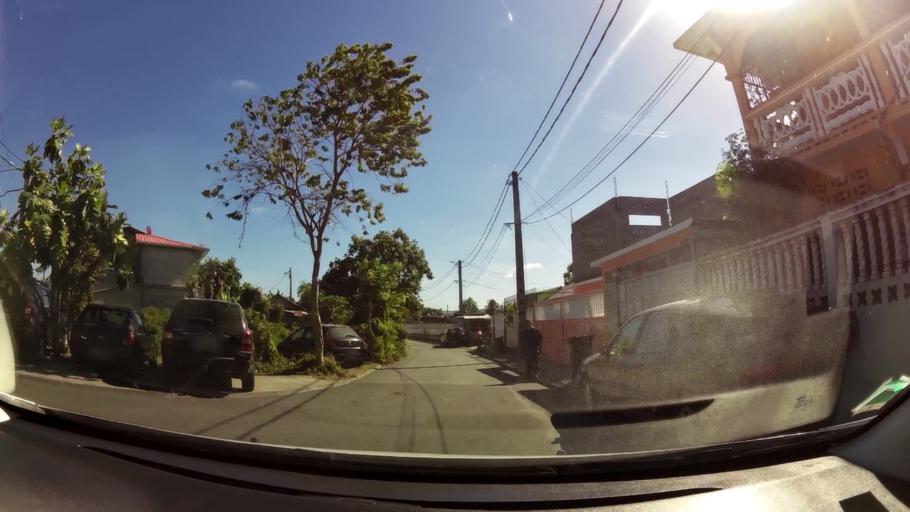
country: YT
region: Pamandzi
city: Pamandzi
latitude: -12.7862
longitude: 45.2730
